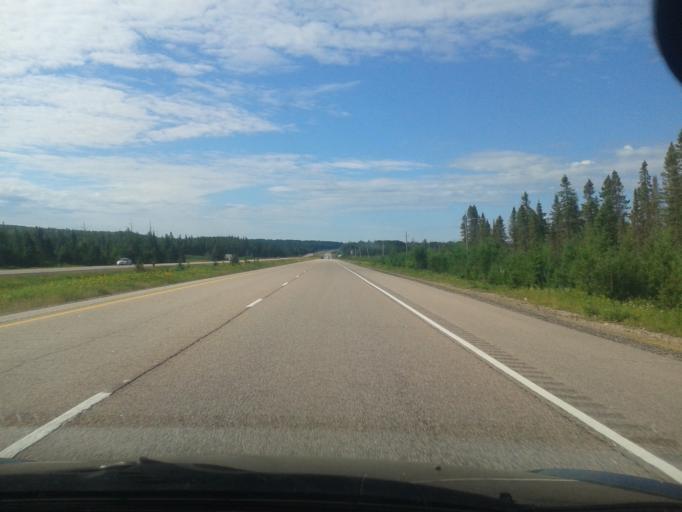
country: CA
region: Ontario
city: Powassan
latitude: 45.9356
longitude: -79.3649
